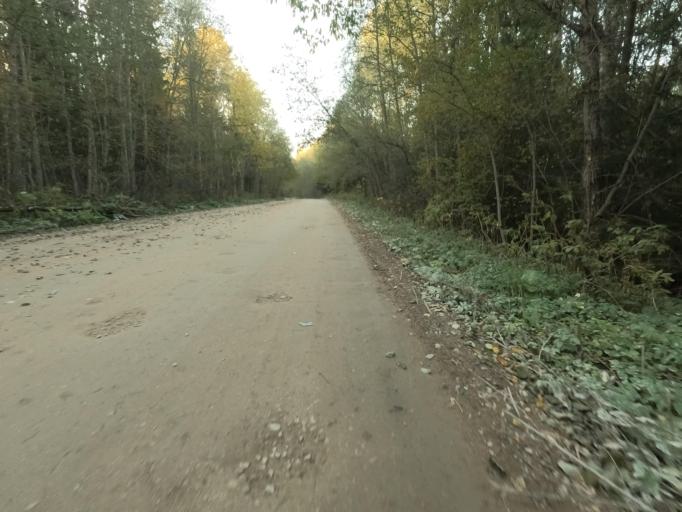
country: RU
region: Leningrad
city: Lyuban'
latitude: 59.0048
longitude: 31.0955
